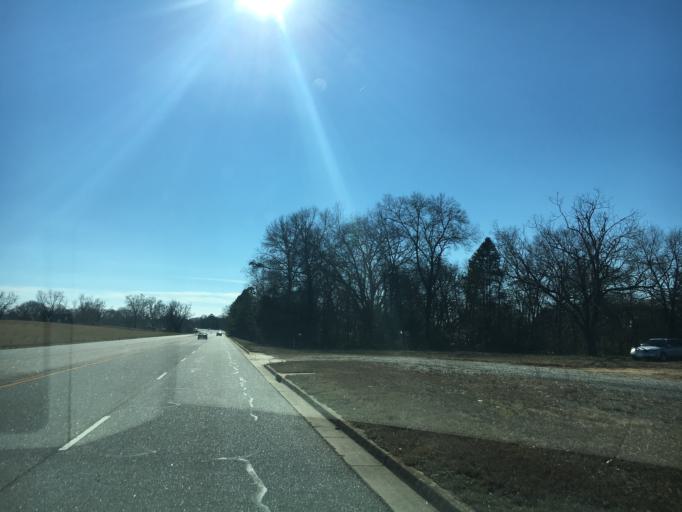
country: US
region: South Carolina
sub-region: Anderson County
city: Iva
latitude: 34.3837
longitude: -82.6939
